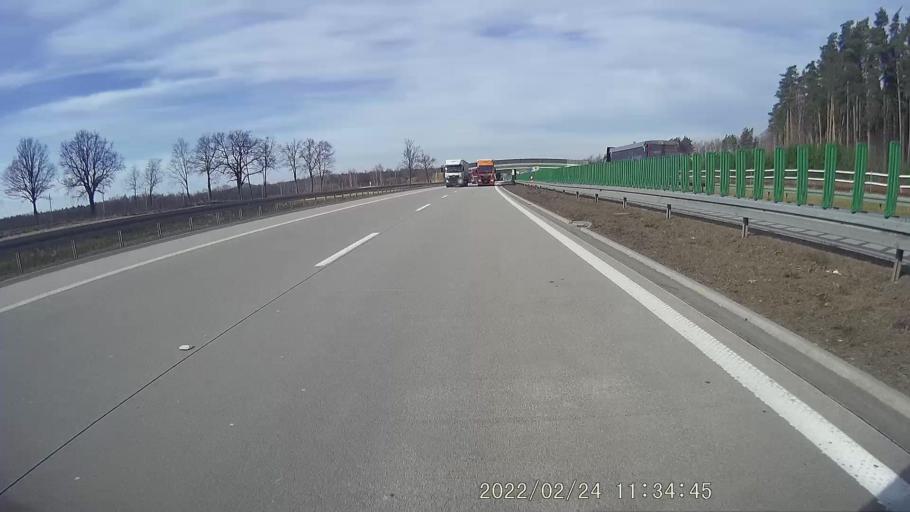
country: PL
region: Lower Silesian Voivodeship
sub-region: Powiat polkowicki
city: Przemkow
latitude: 51.5243
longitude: 15.7846
